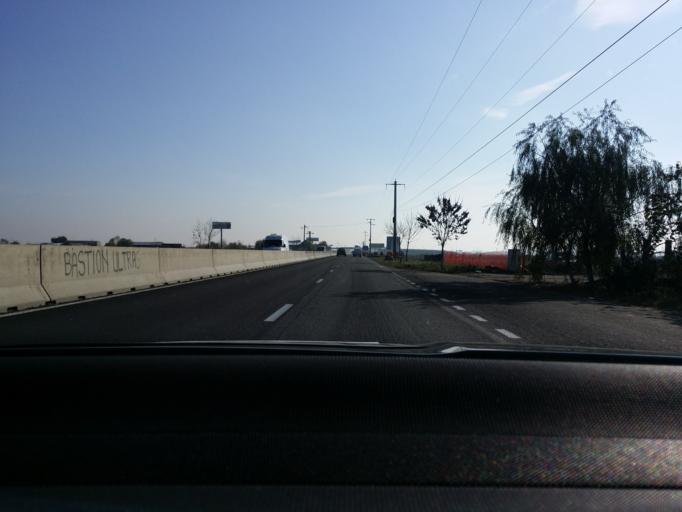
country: RO
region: Prahova
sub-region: Comuna Paulesti
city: Paulesti
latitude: 44.9757
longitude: 25.9456
